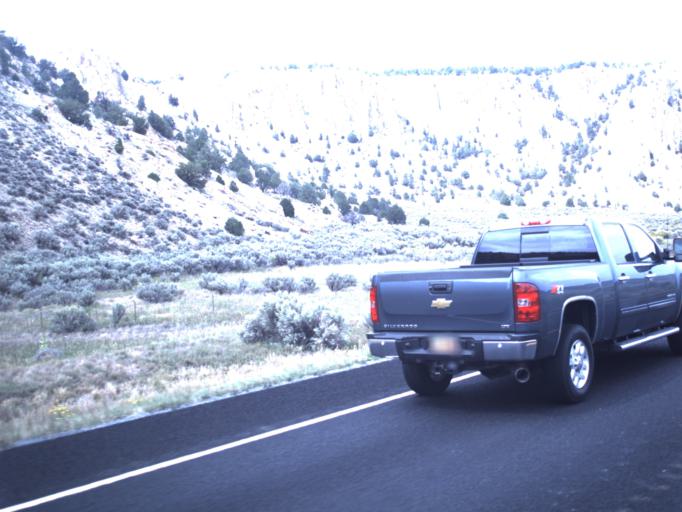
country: US
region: Utah
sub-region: Garfield County
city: Panguitch
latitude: 38.0296
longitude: -112.3576
